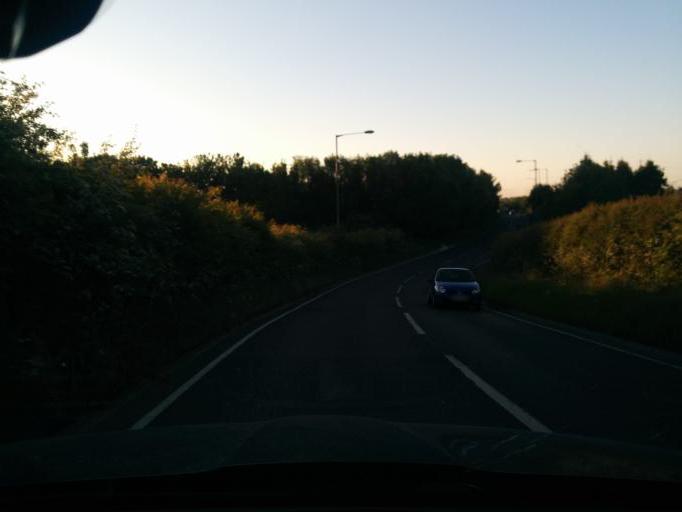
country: GB
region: England
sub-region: Northumberland
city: Choppington
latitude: 55.1415
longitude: -1.6002
